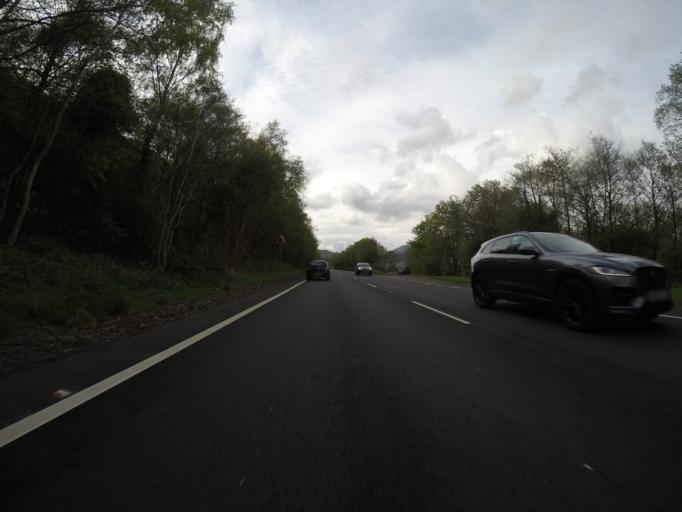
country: GB
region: Scotland
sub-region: Argyll and Bute
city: Helensburgh
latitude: 56.1374
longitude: -4.6596
